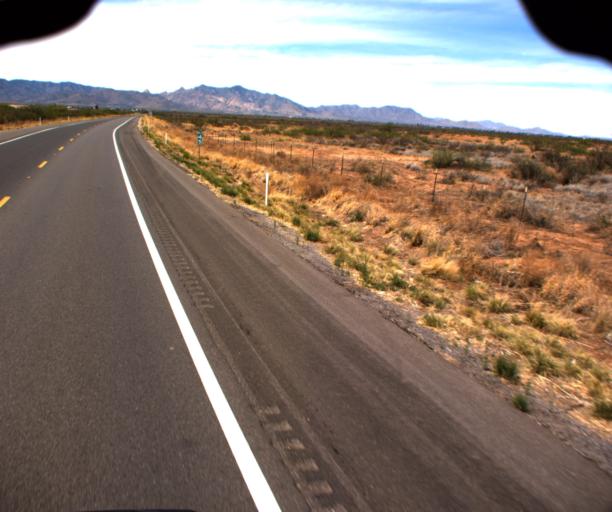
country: US
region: Arizona
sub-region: Cochise County
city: Tombstone
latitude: 31.9037
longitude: -109.7968
